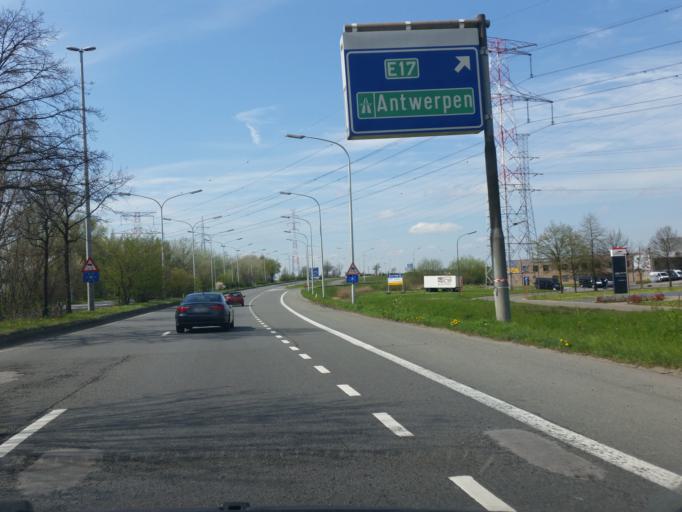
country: BE
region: Flanders
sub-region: Provincie Oost-Vlaanderen
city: Temse
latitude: 51.1371
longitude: 4.1778
